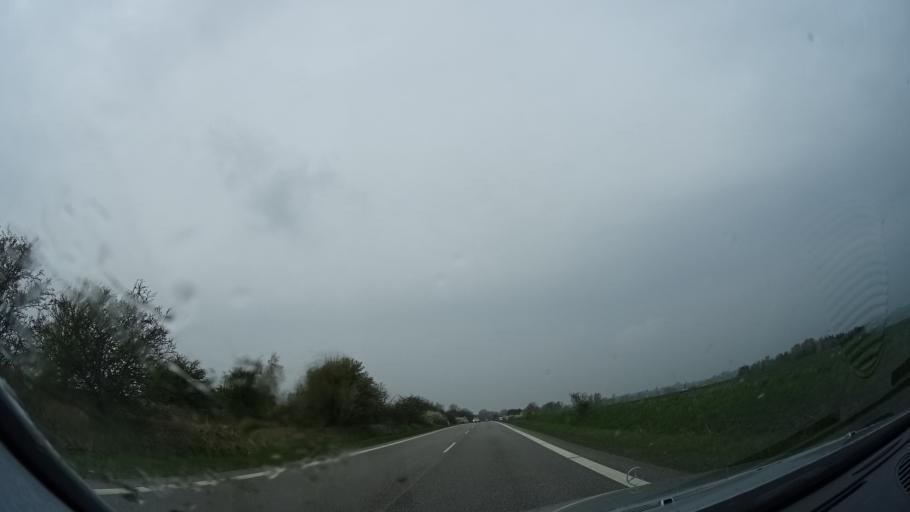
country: DK
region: Zealand
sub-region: Holbaek Kommune
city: Holbaek
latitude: 55.7184
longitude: 11.6447
